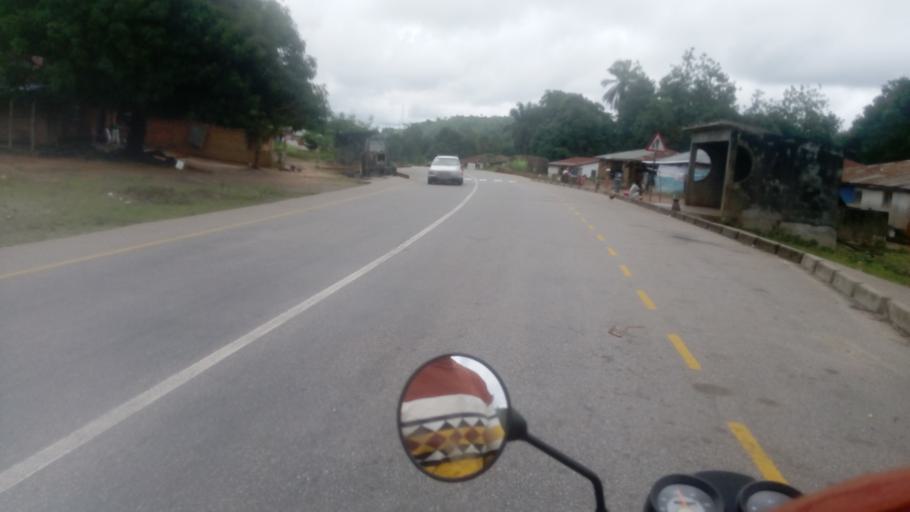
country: SL
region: Northern Province
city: Masaka
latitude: 8.6457
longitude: -11.7594
